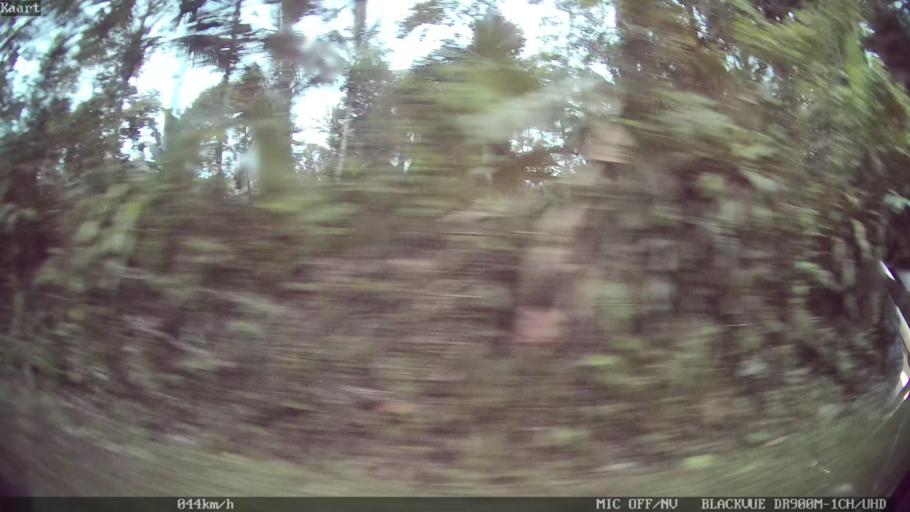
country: ID
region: Bali
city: Banjar Geriana Kangin
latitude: -8.3953
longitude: 115.4419
